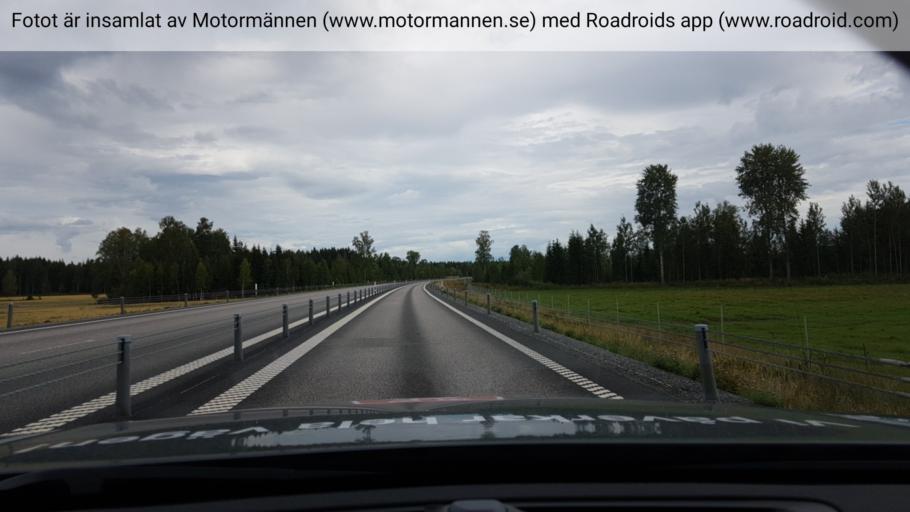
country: SE
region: Uppsala
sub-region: Heby Kommun
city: Heby
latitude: 60.0035
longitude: 16.8517
